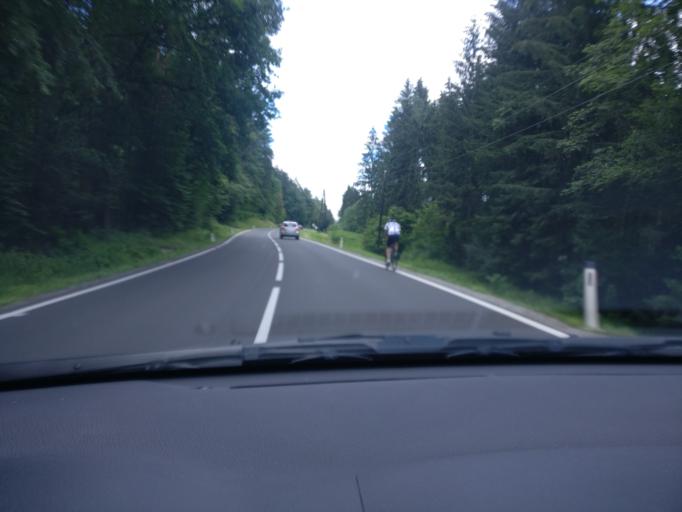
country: AT
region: Styria
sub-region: Politischer Bezirk Weiz
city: Oberrettenbach
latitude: 47.1589
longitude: 15.7749
